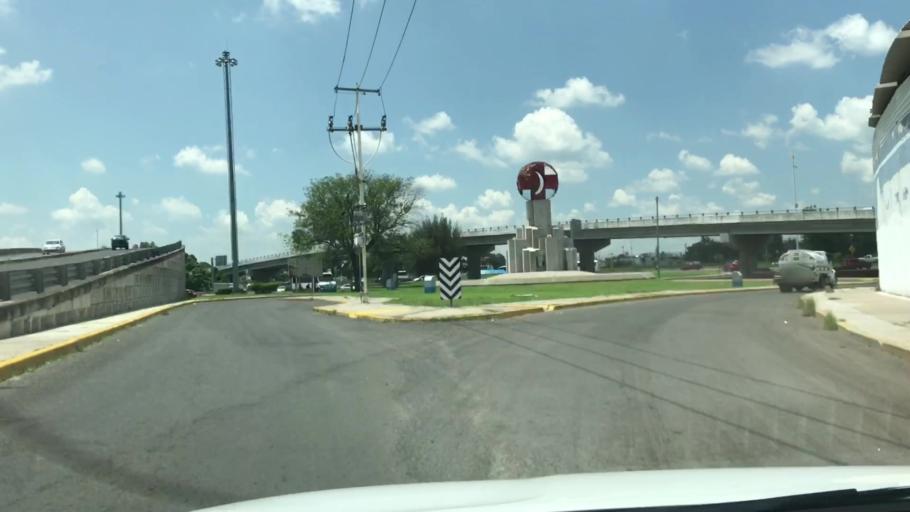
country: MX
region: Guanajuato
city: Celaya
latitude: 20.5182
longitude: -100.8381
